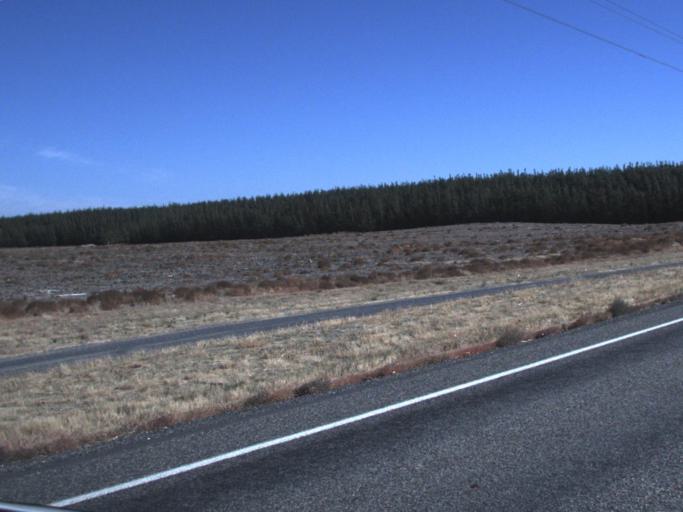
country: US
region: Washington
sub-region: Walla Walla County
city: Burbank
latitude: 46.2151
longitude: -118.8912
